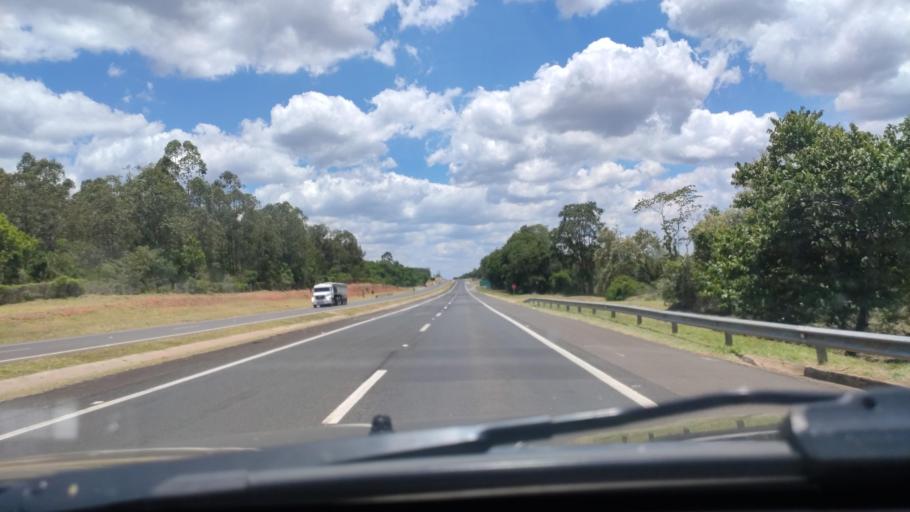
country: BR
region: Sao Paulo
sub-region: Duartina
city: Duartina
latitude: -22.5092
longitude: -49.2971
